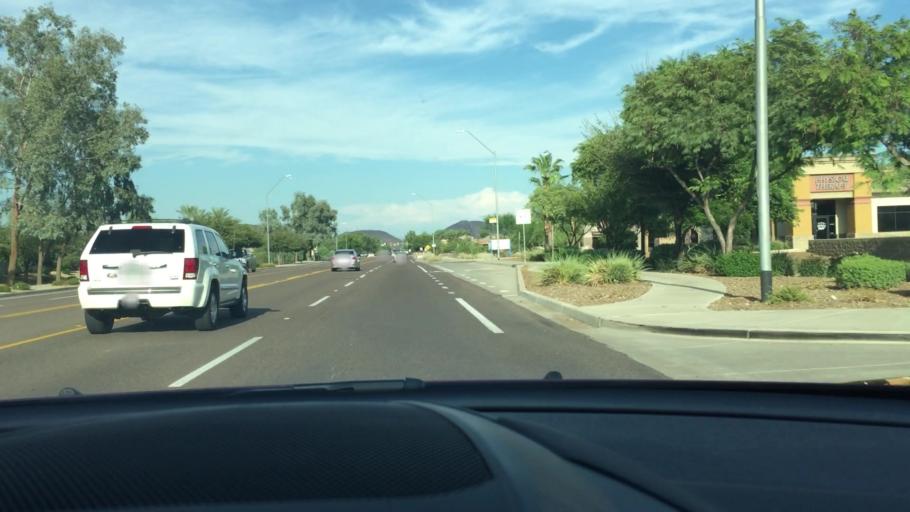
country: US
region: Arizona
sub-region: Maricopa County
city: Sun City
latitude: 33.6816
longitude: -112.2256
